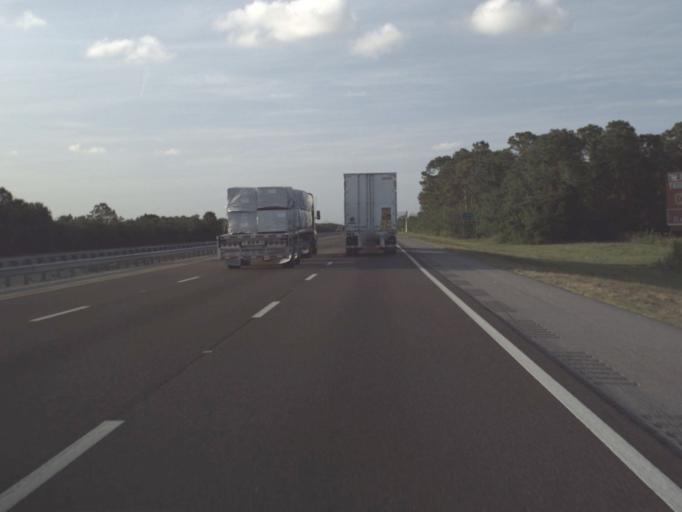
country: US
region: Florida
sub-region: Brevard County
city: Port Saint John
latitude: 28.5300
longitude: -80.8516
